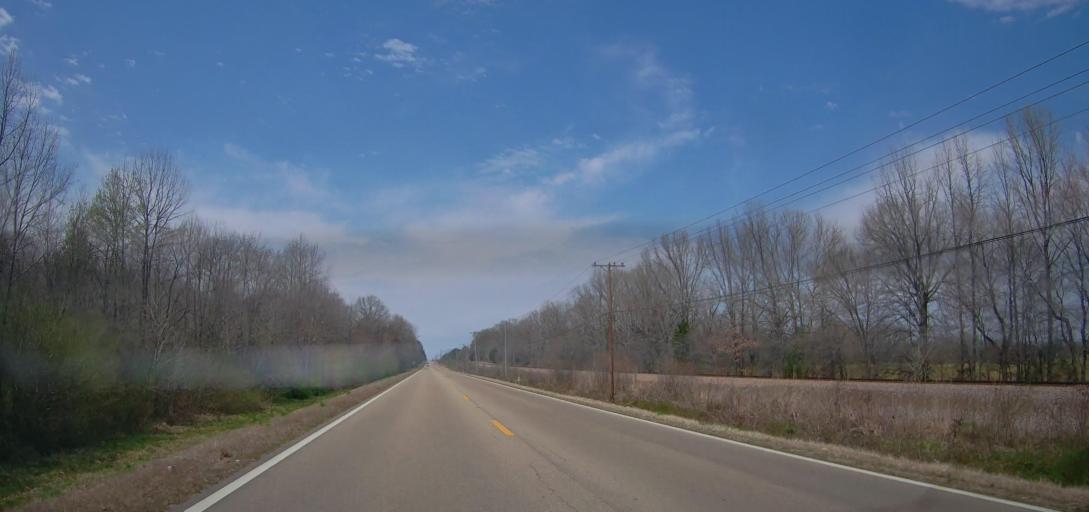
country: US
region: Mississippi
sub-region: Union County
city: New Albany
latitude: 34.5230
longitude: -89.0603
